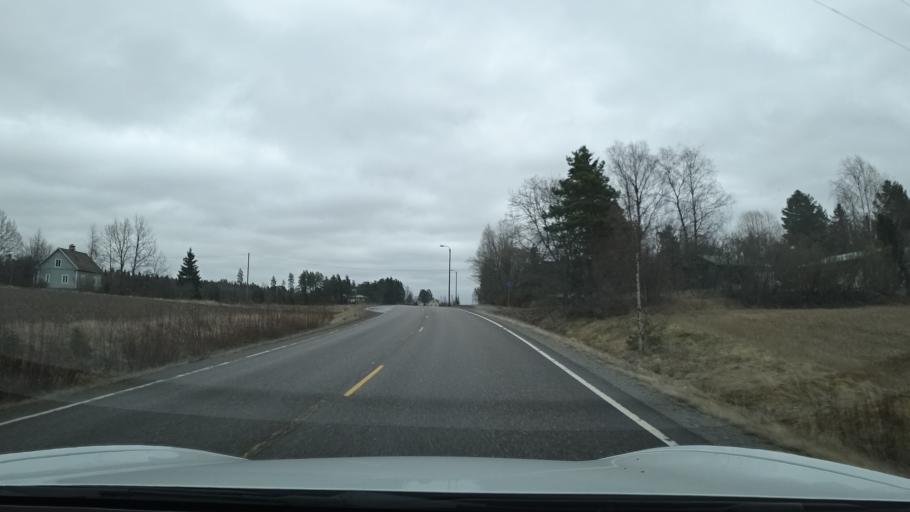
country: FI
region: Uusimaa
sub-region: Porvoo
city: Askola
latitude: 60.4959
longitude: 25.5031
